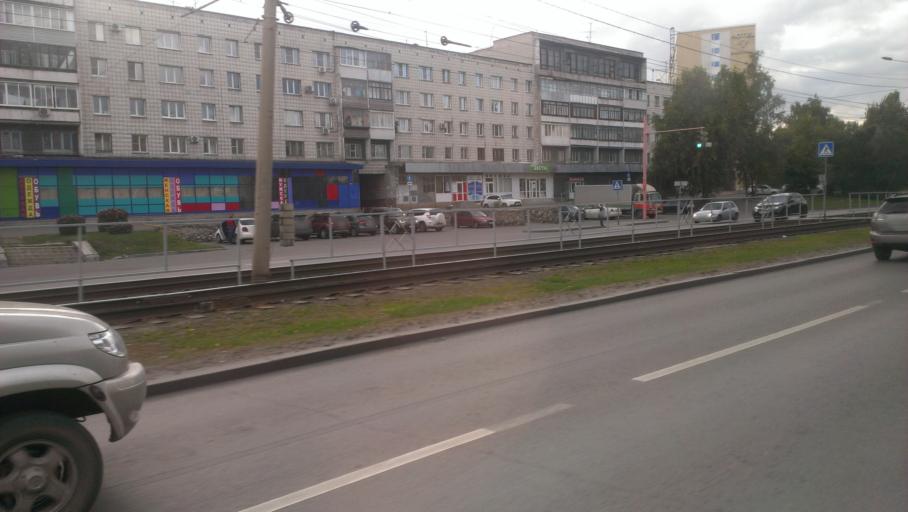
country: RU
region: Altai Krai
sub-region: Gorod Barnaulskiy
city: Barnaul
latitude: 53.3465
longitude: 83.7645
